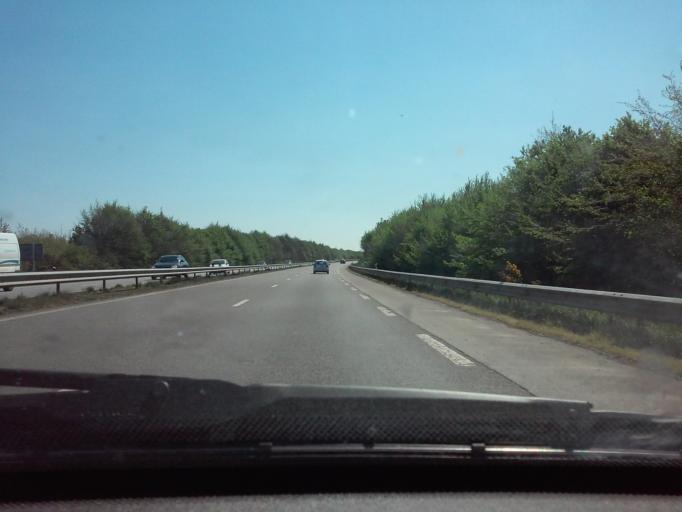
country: FR
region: Brittany
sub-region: Departement d'Ille-et-Vilaine
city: Saint-Domineuc
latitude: 48.3526
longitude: -1.8654
